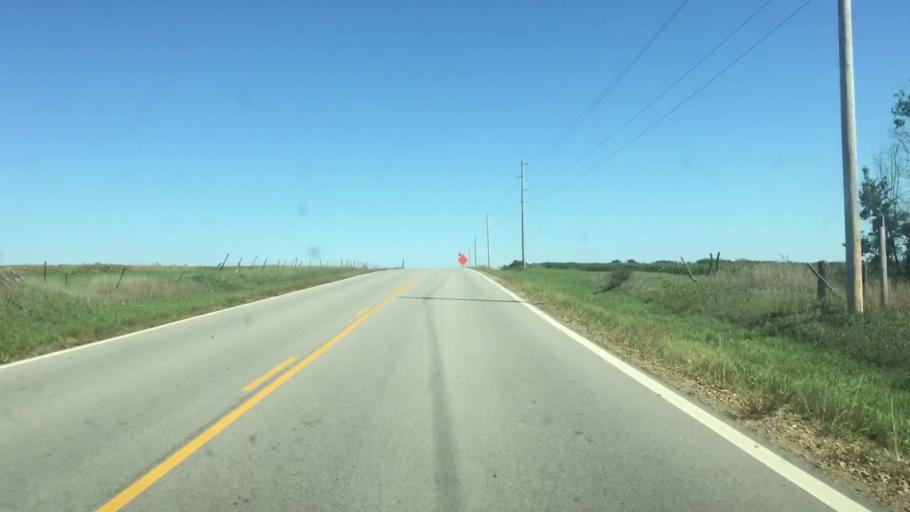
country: US
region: Kansas
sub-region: Jackson County
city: Holton
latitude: 39.5949
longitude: -95.6863
